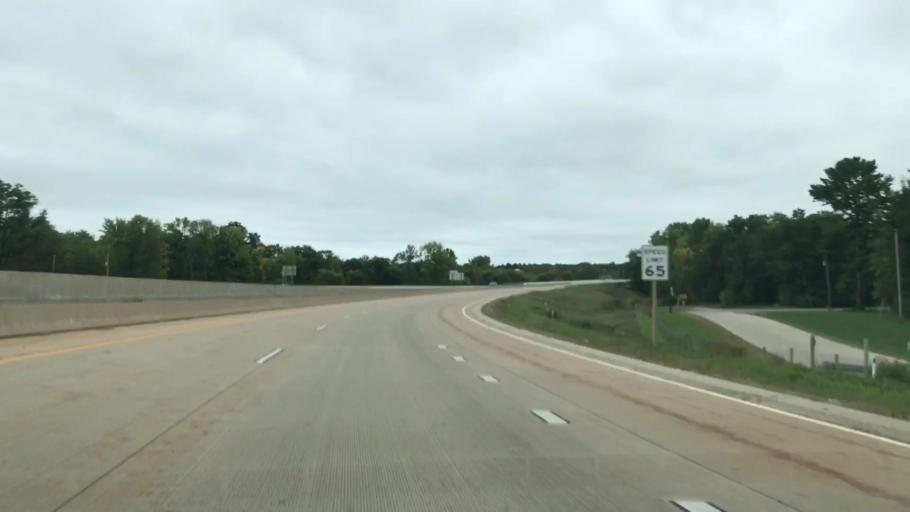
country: US
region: Wisconsin
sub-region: Oconto County
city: Oconto
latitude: 44.8902
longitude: -87.8955
